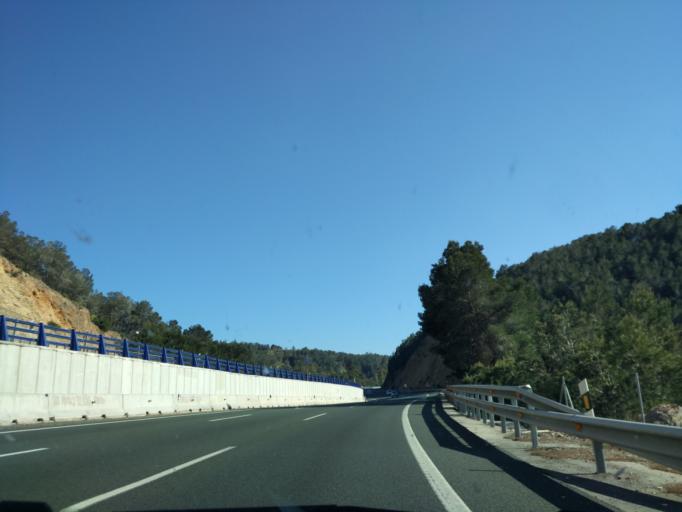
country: ES
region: Murcia
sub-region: Murcia
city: Murcia
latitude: 37.9023
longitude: -1.1439
